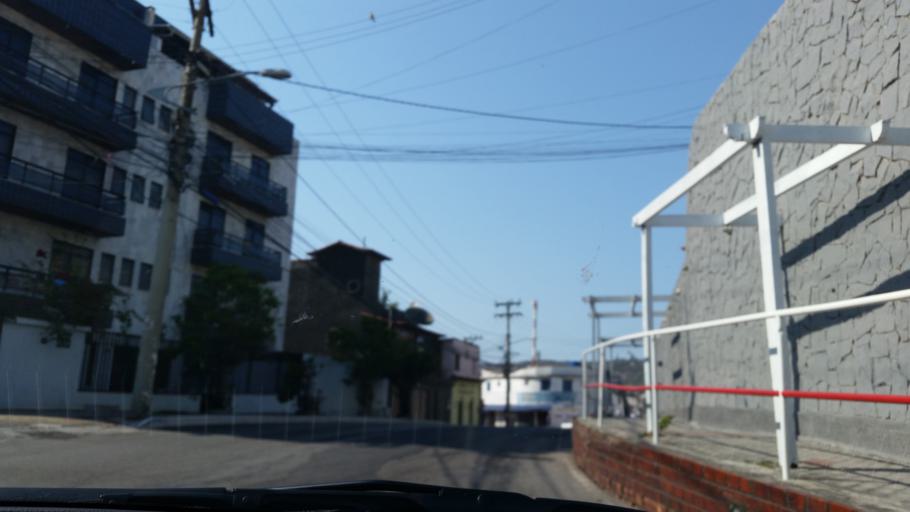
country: BR
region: Rio de Janeiro
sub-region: Arraial Do Cabo
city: Arraial do Cabo
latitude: -22.9656
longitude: -42.0290
